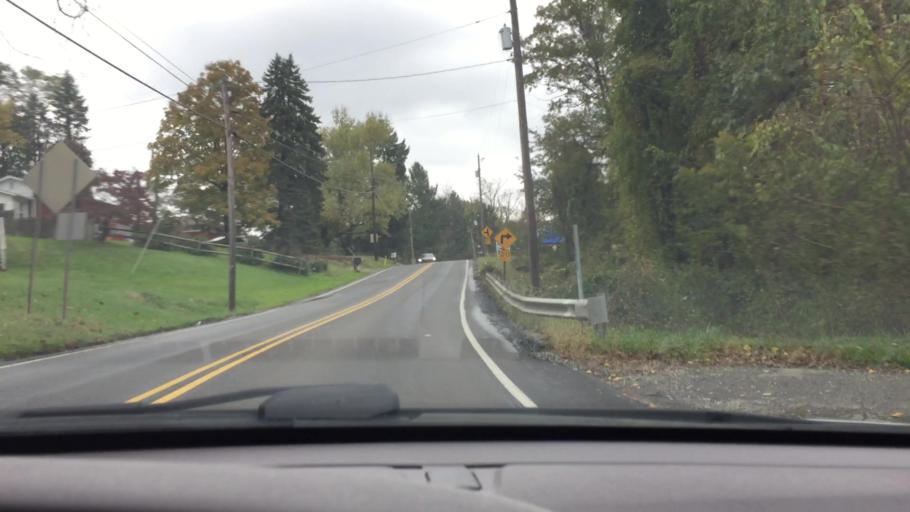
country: US
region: Pennsylvania
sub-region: Washington County
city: Speers
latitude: 40.1049
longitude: -79.8917
